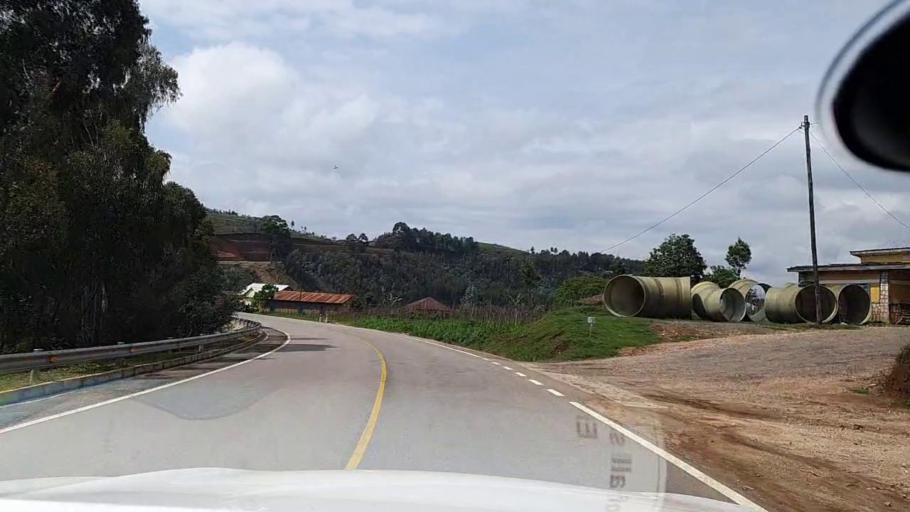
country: RW
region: Southern Province
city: Nzega
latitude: -2.4887
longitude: 29.5120
